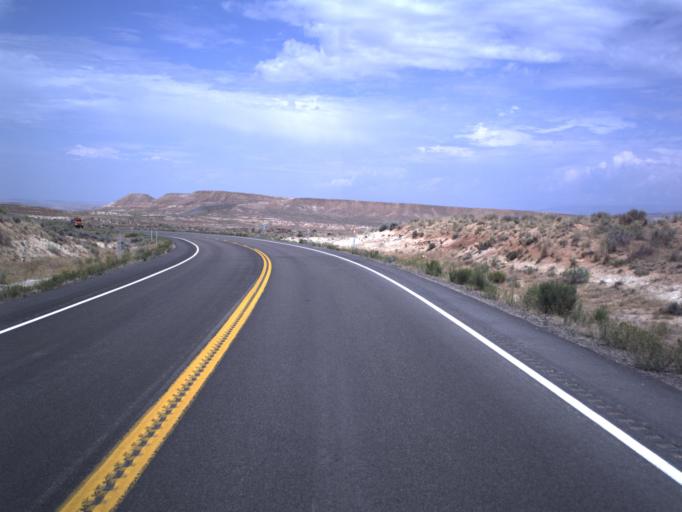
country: US
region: Utah
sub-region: Uintah County
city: Naples
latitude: 40.2611
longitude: -109.4362
